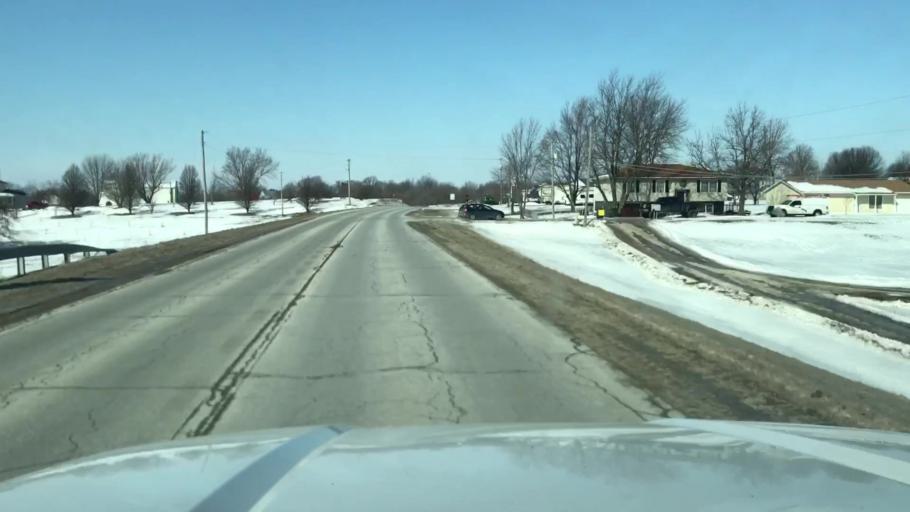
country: US
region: Missouri
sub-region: Andrew County
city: Savannah
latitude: 39.9495
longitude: -94.8437
